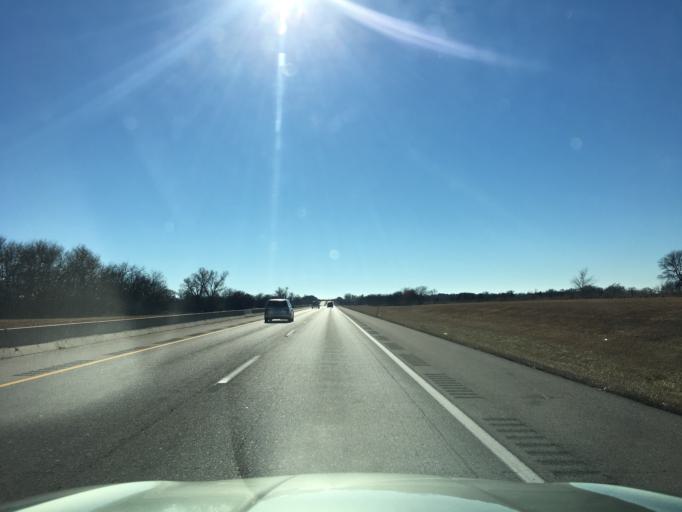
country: US
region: Kansas
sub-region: Sumner County
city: Wellington
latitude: 37.0955
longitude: -97.3387
